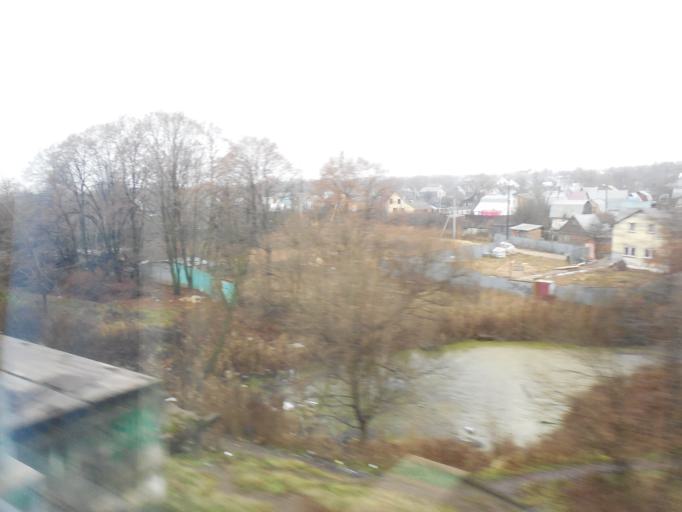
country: RU
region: Moskovskaya
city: Vidnoye
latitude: 55.5175
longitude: 37.7072
